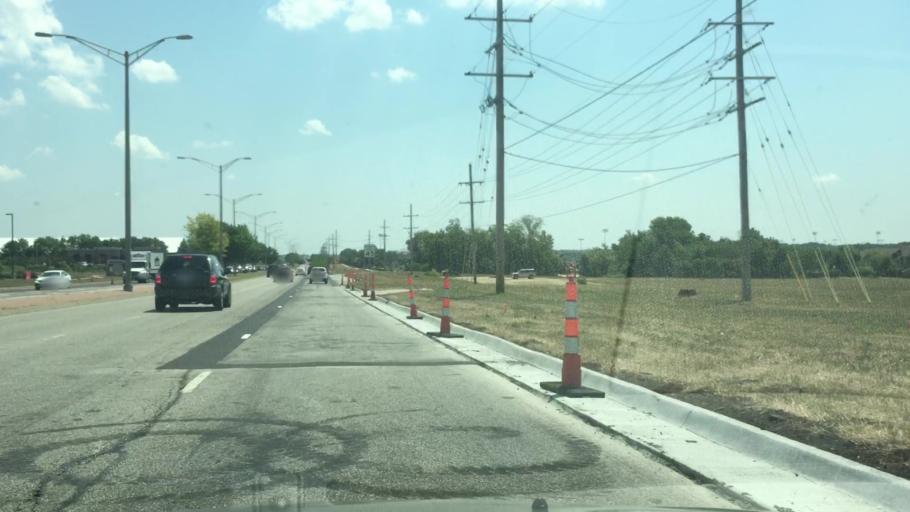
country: US
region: Kansas
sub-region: Johnson County
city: Lenexa
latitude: 38.8836
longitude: -94.7000
